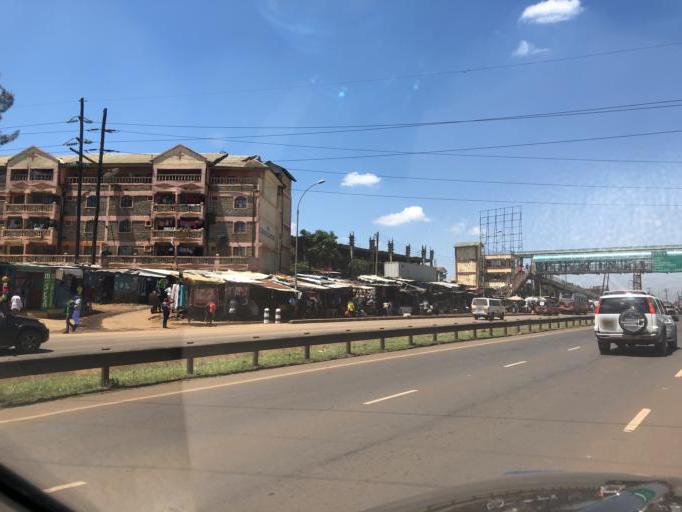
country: KE
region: Kiambu
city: Kiambu
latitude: -1.2163
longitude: 36.8953
